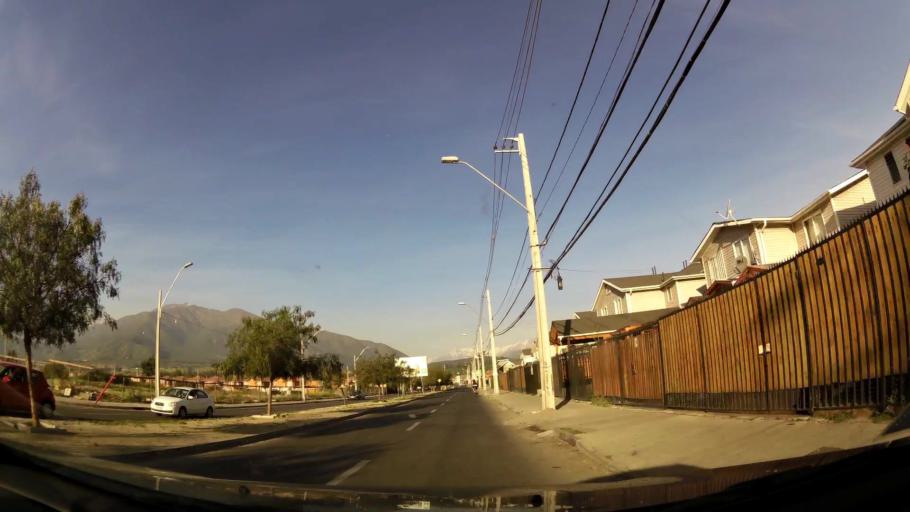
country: CL
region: Santiago Metropolitan
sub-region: Provincia de Cordillera
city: Puente Alto
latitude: -33.5963
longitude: -70.5546
